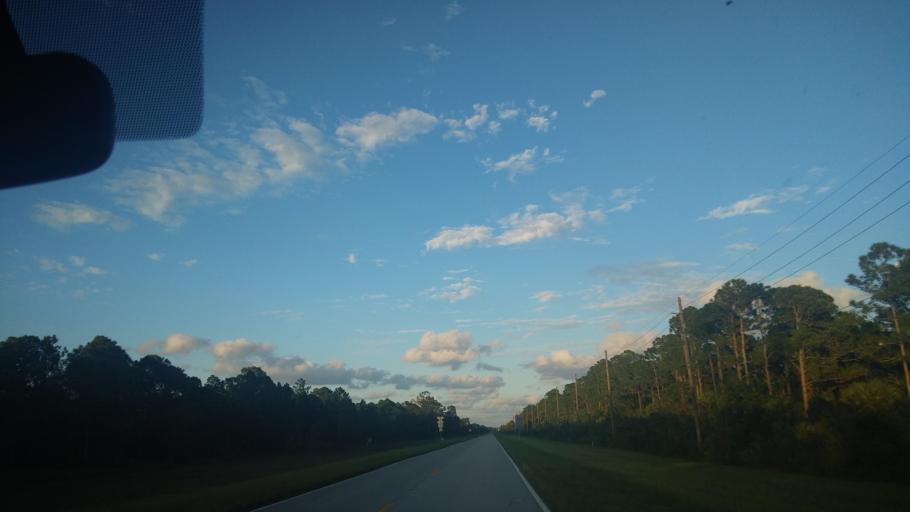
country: US
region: Florida
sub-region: Indian River County
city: Fellsmere
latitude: 27.7512
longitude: -80.6263
